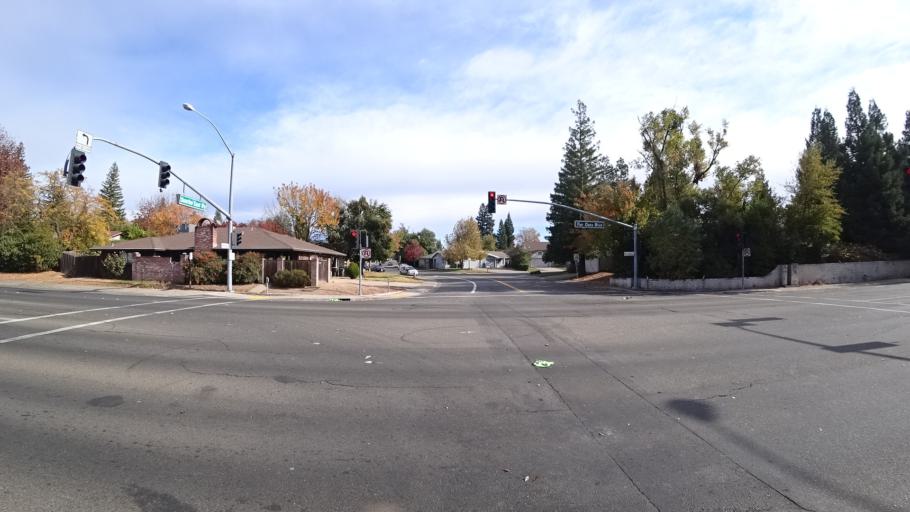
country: US
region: California
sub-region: Sacramento County
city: Fair Oaks
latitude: 38.6724
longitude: -121.2623
